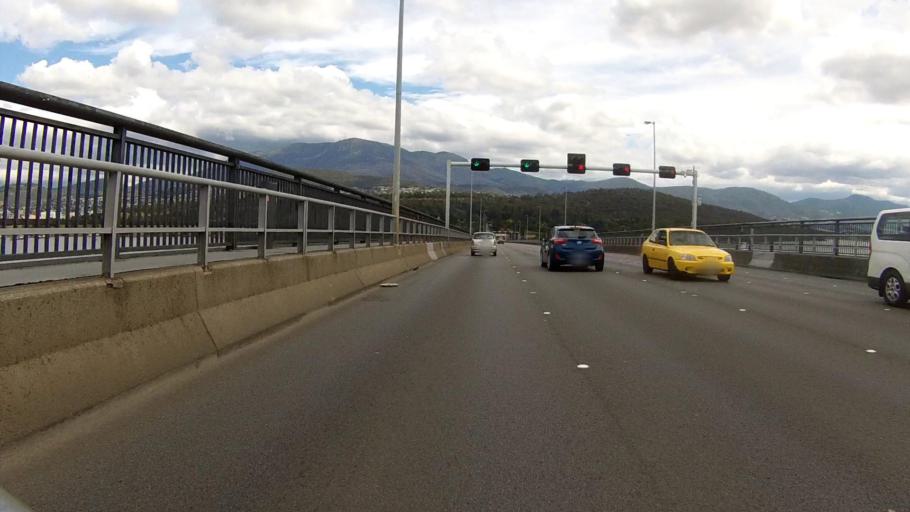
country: AU
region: Tasmania
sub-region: Hobart
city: Hobart
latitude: -42.8653
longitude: 147.3435
